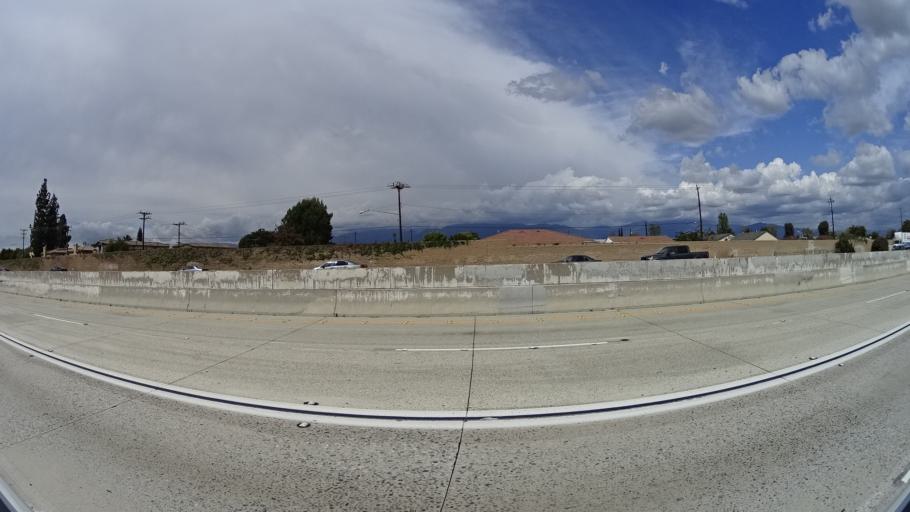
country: US
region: California
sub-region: Los Angeles County
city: Rosemead
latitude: 34.0722
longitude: -118.0645
